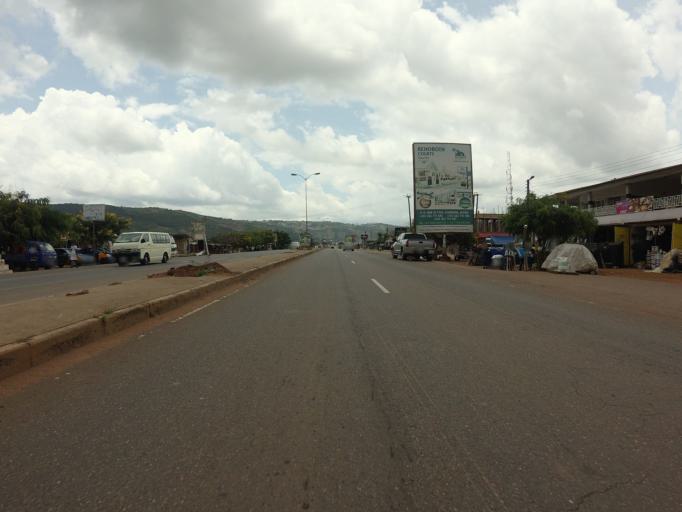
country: GH
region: Eastern
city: Aburi
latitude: 5.7664
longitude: -0.1801
